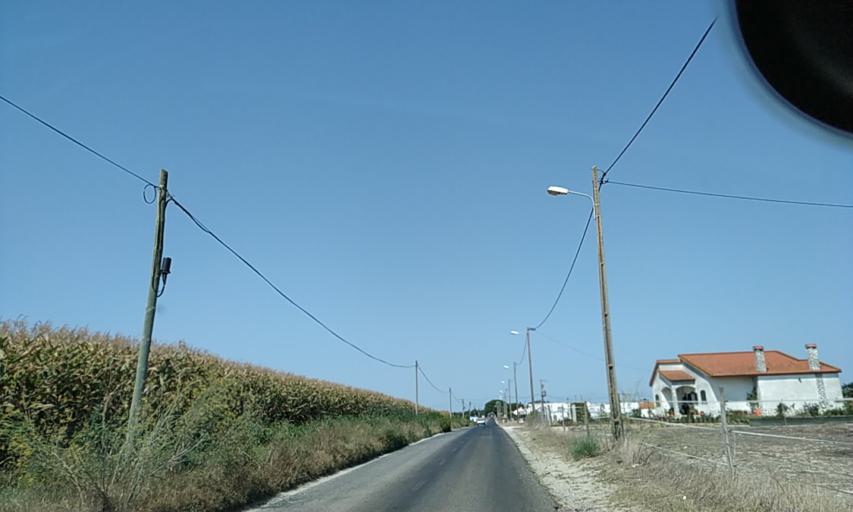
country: PT
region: Santarem
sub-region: Benavente
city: Poceirao
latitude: 38.7081
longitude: -8.7184
